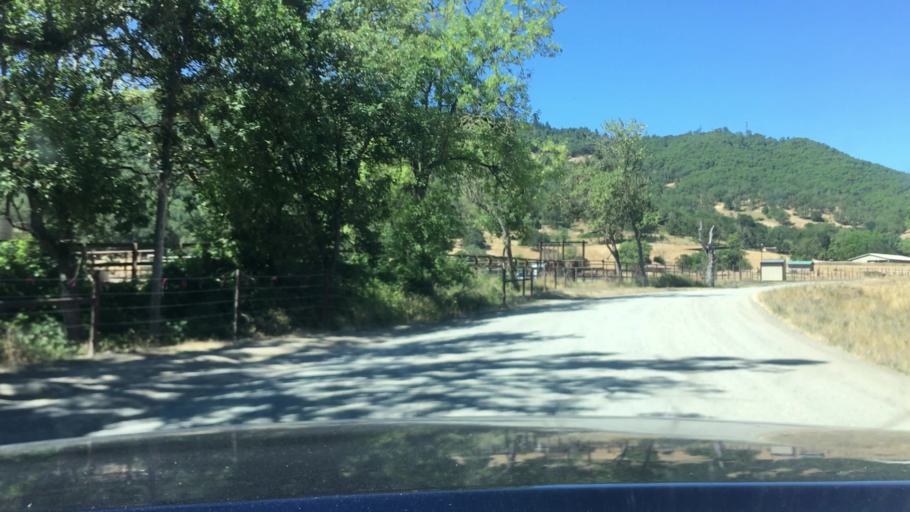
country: US
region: Oregon
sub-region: Douglas County
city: Winston
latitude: 43.1359
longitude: -123.4326
